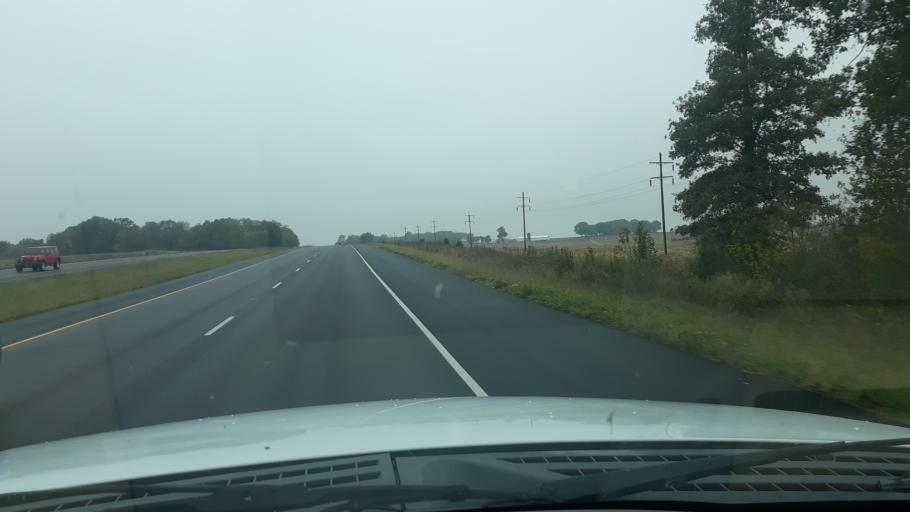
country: US
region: Illinois
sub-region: Saline County
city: Eldorado
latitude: 37.7956
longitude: -88.4707
